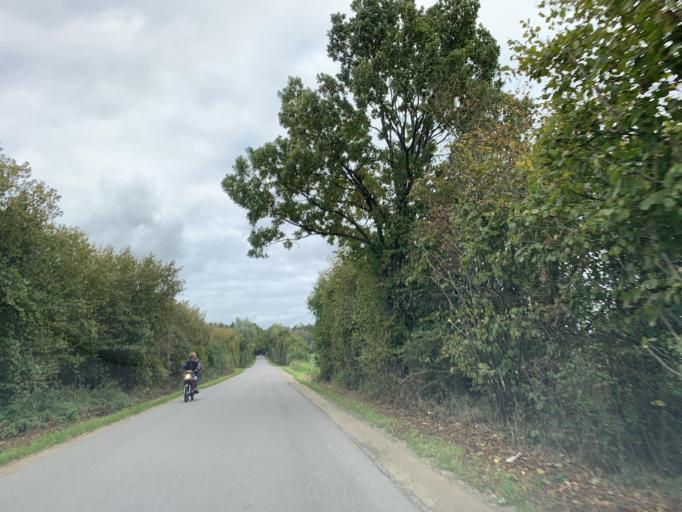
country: DE
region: Mecklenburg-Vorpommern
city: Blankensee
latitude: 53.4266
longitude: 13.2642
